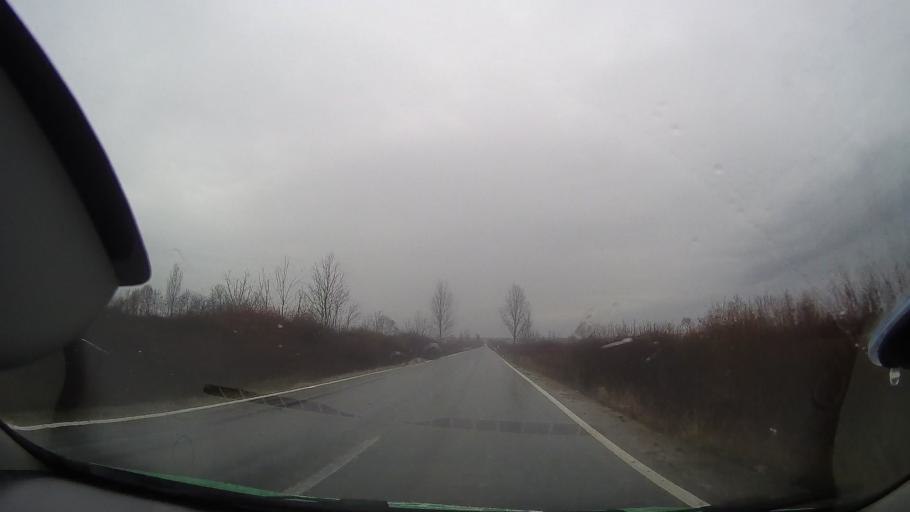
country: RO
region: Bihor
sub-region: Comuna Tinca
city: Tinca
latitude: 46.7479
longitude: 21.9382
